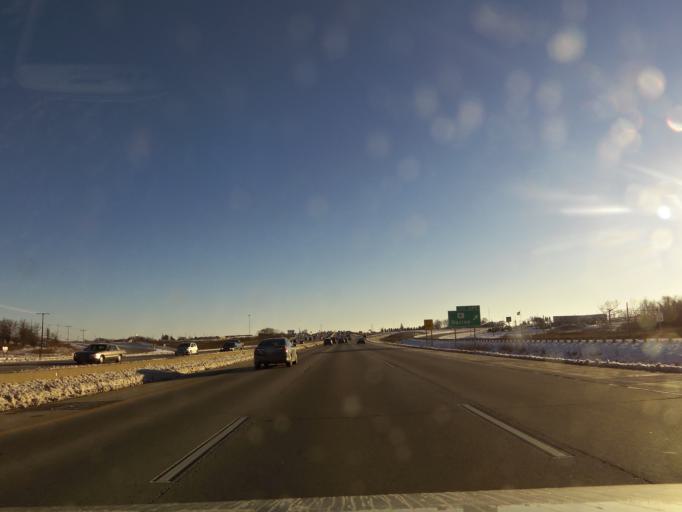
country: US
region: Wisconsin
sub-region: Racine County
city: Caledonia
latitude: 42.7856
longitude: -87.9538
